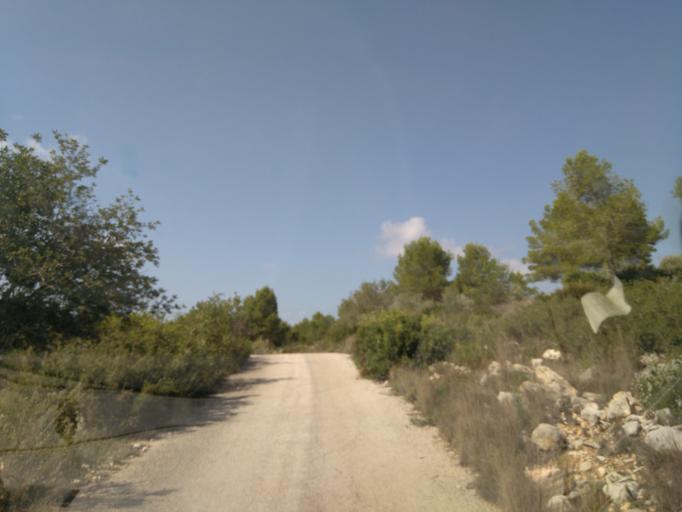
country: ES
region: Valencia
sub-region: Provincia de Valencia
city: Tous
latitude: 39.1778
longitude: -0.6230
